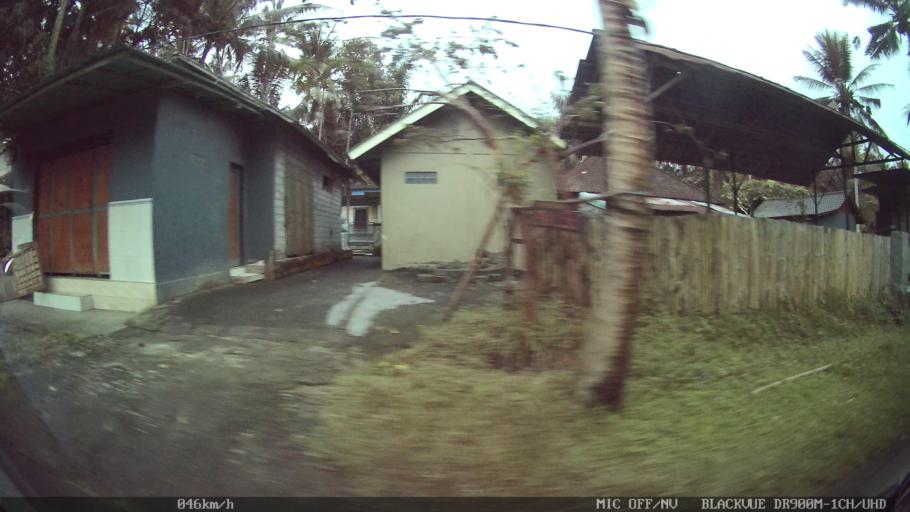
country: ID
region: Bali
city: Pegongan
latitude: -8.4726
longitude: 115.2331
